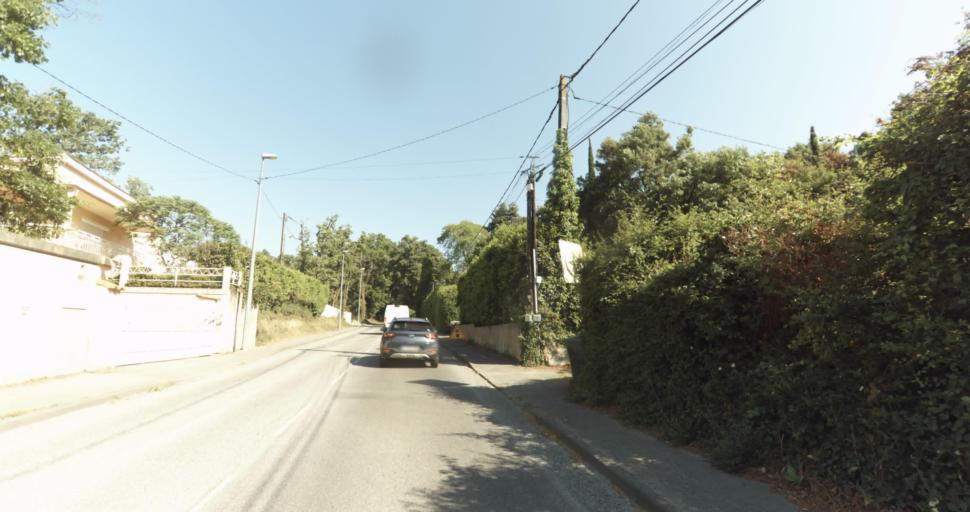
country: FR
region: Midi-Pyrenees
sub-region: Departement de la Haute-Garonne
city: Plaisance-du-Touch
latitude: 43.5719
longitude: 1.2929
